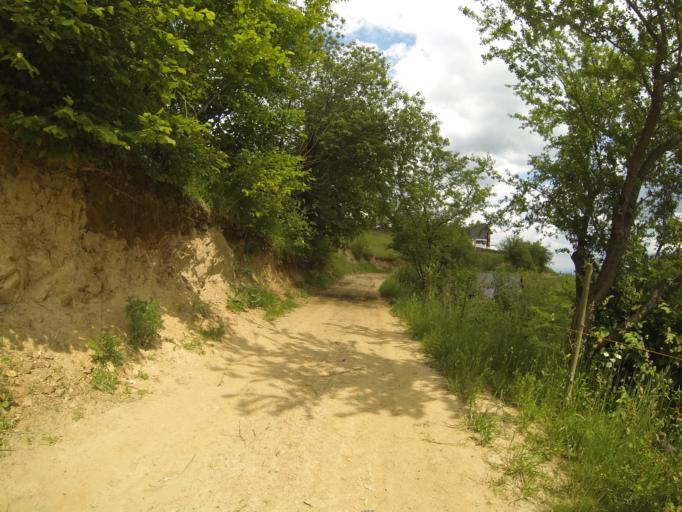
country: RO
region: Brasov
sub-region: Comuna Poiana Marului
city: Poiana Marului
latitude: 45.6380
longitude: 25.2961
